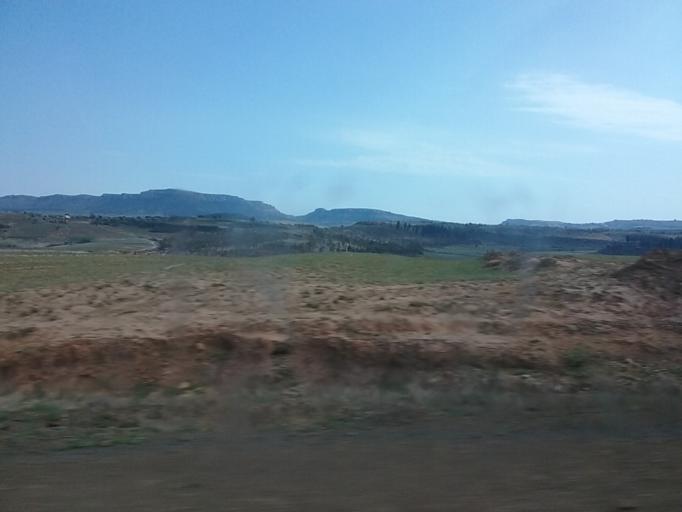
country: LS
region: Berea
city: Teyateyaneng
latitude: -29.0848
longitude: 27.9207
